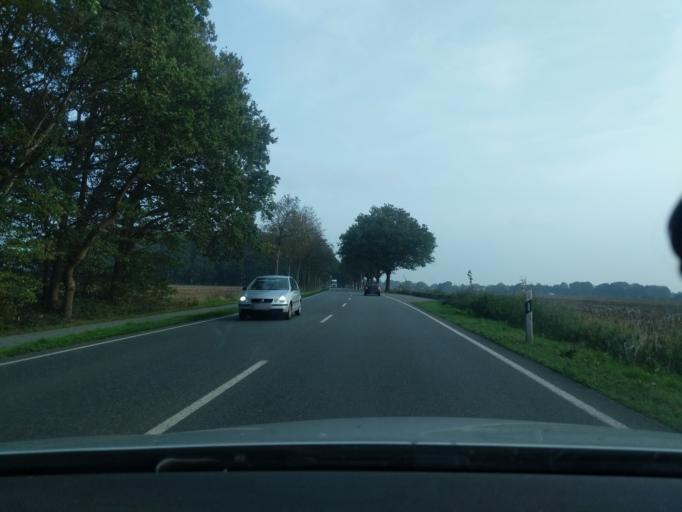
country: DE
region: Lower Saxony
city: Heinbockel
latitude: 53.5955
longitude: 9.3292
